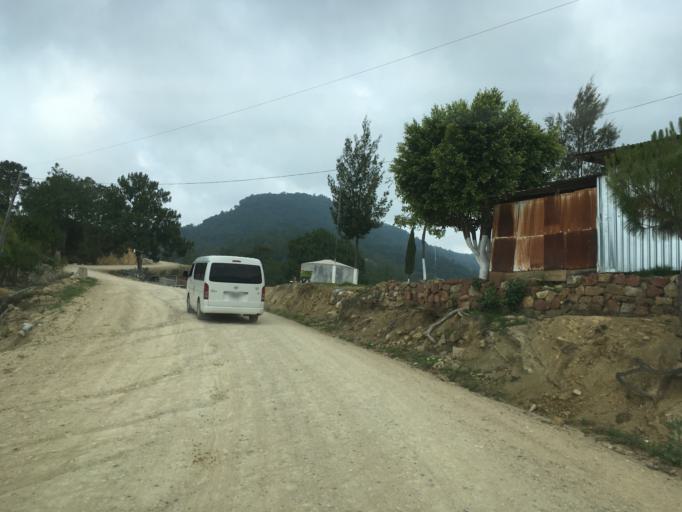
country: MX
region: Oaxaca
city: Santiago Tilantongo
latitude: 17.1973
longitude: -97.2838
